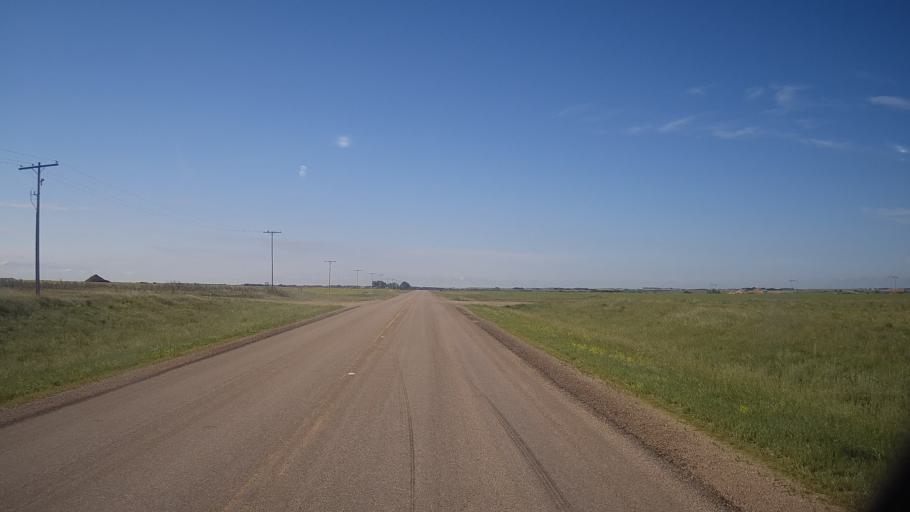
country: CA
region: Saskatchewan
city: Watrous
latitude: 51.7299
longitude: -105.3574
